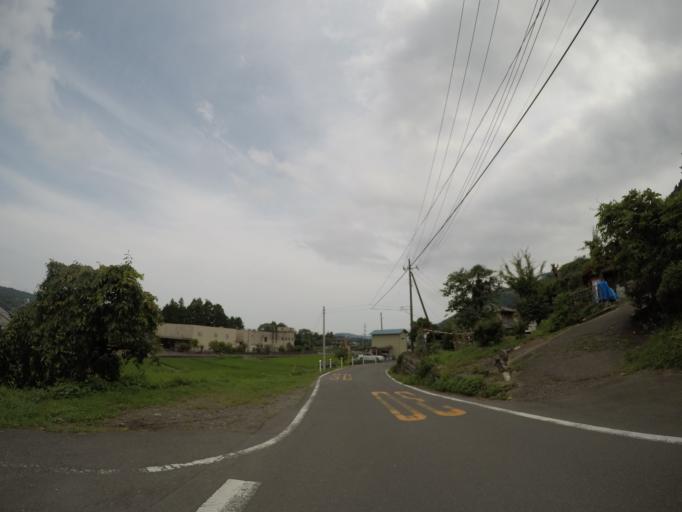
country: JP
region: Shizuoka
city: Fujinomiya
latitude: 35.2529
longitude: 138.5531
